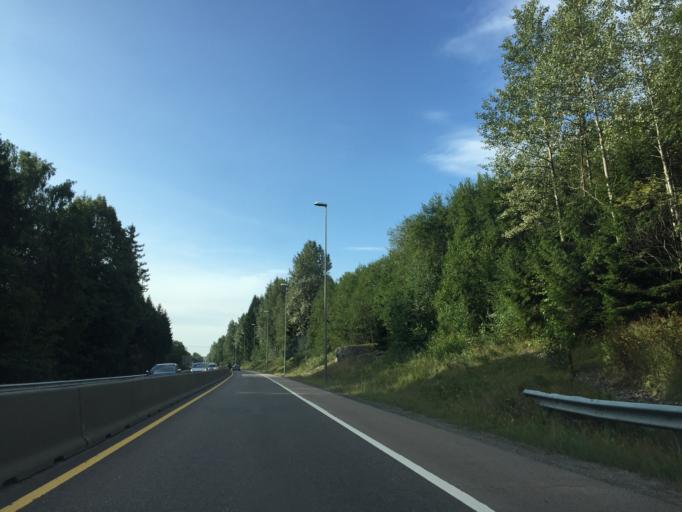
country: NO
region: Akershus
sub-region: Ski
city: Ski
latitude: 59.7368
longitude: 10.7823
